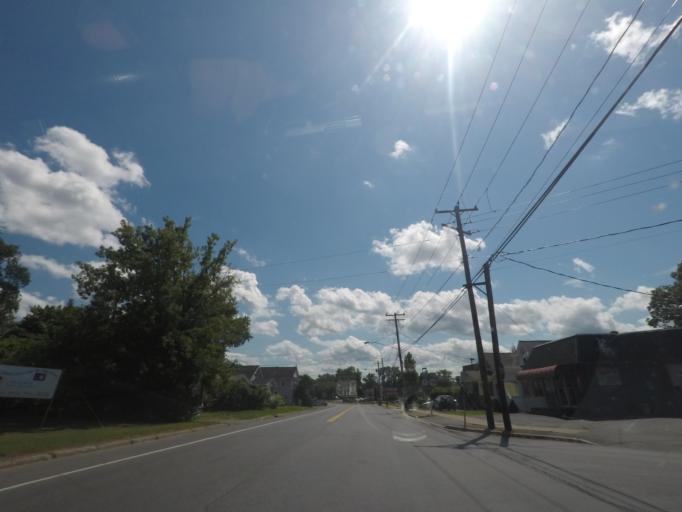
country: US
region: New York
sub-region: Schenectady County
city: Rotterdam
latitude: 42.7879
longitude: -73.9703
